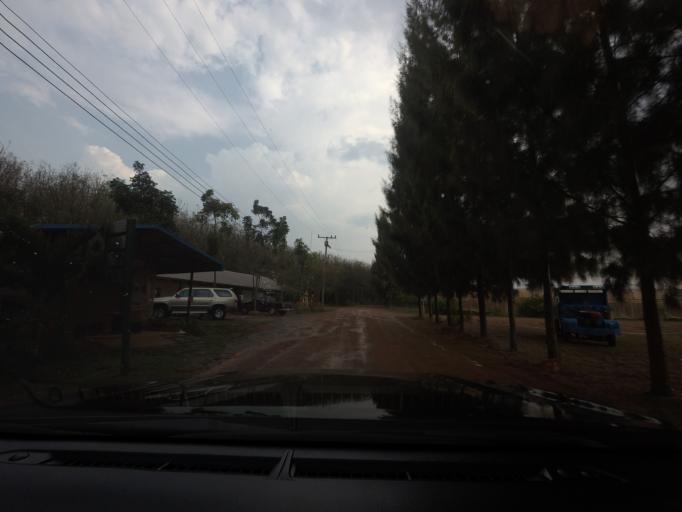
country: TH
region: Nakhon Ratchasima
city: Wang Nam Khiao
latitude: 14.4139
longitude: 101.7384
